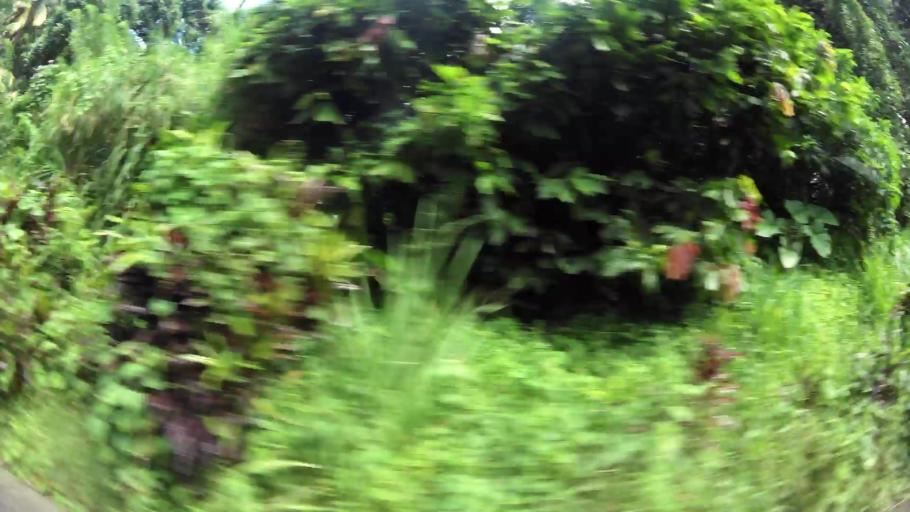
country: MQ
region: Martinique
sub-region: Martinique
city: Le Morne-Rouge
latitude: 14.7628
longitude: -61.1549
